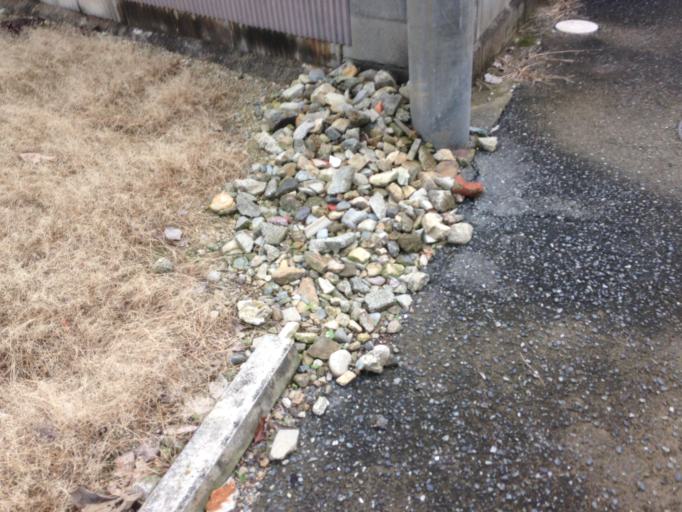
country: JP
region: Hyogo
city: Tatsunocho-tominaga
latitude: 34.8659
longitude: 134.5422
